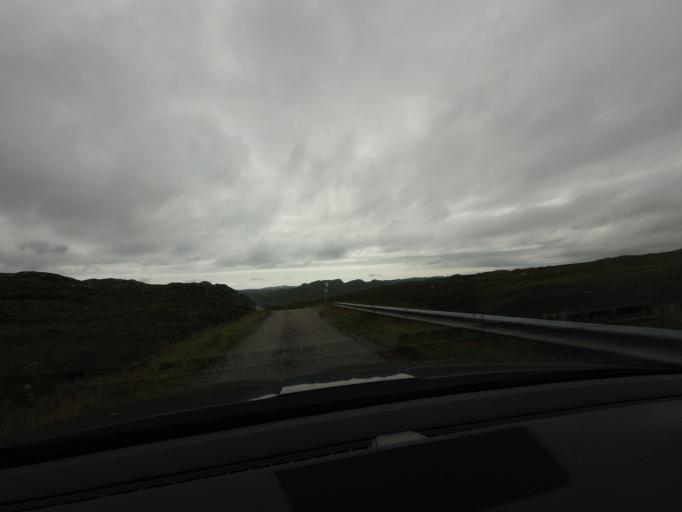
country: GB
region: Scotland
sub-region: Highland
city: Ullapool
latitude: 58.4456
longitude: -4.9477
